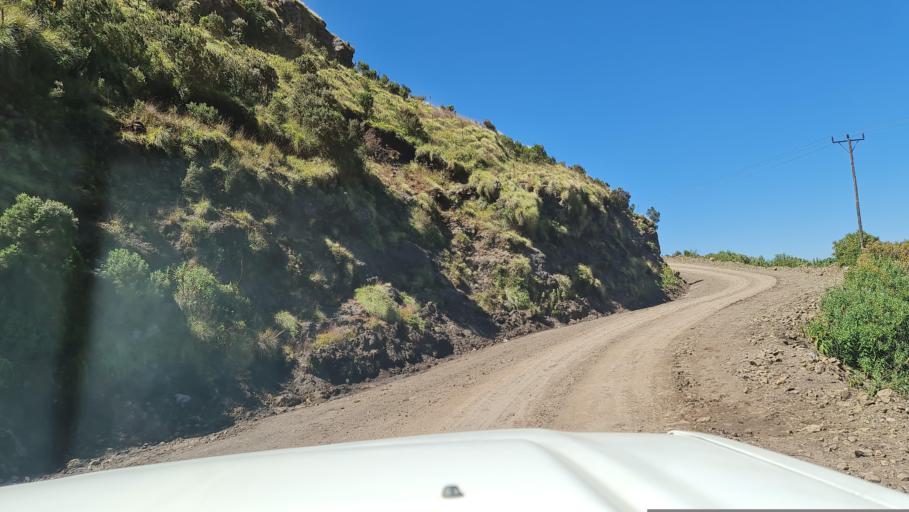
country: ET
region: Amhara
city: Debark'
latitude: 13.2327
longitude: 38.0724
